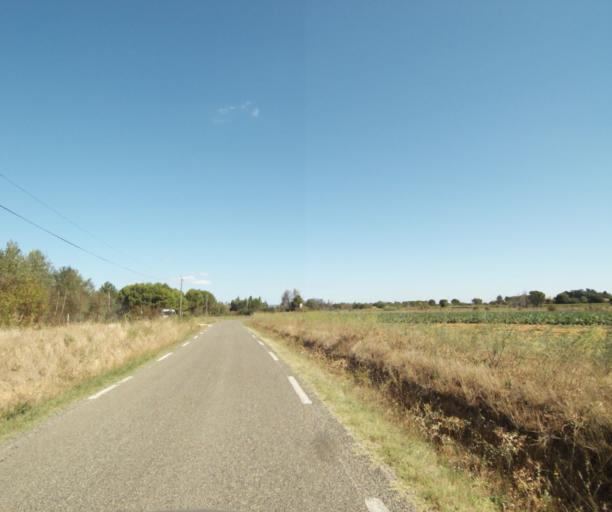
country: FR
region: Languedoc-Roussillon
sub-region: Departement du Gard
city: Bouillargues
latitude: 43.8083
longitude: 4.4282
